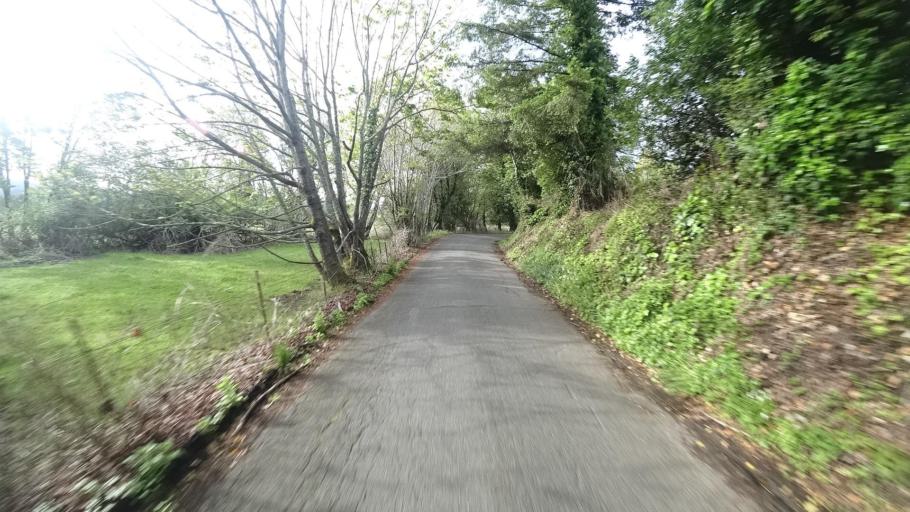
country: US
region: California
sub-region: Humboldt County
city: Blue Lake
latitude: 40.8713
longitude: -124.0047
